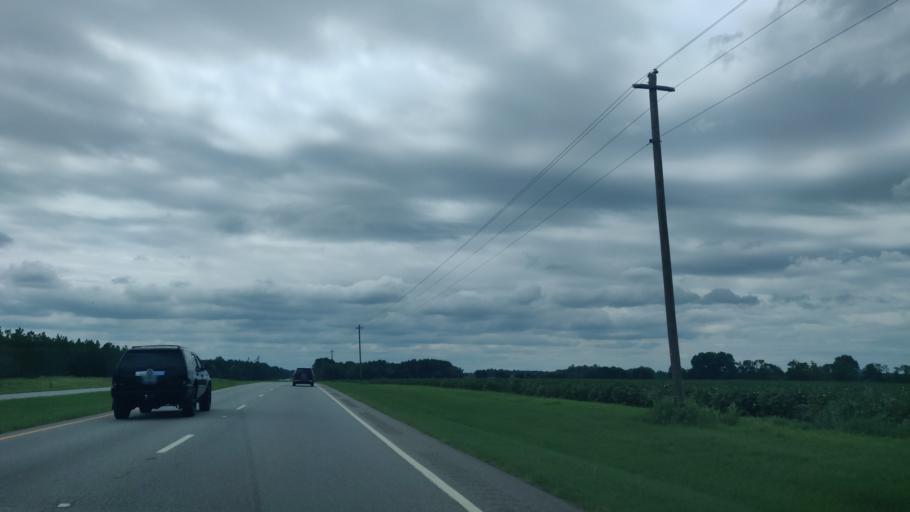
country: US
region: Georgia
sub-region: Terrell County
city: Dawson
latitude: 31.8169
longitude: -84.4574
